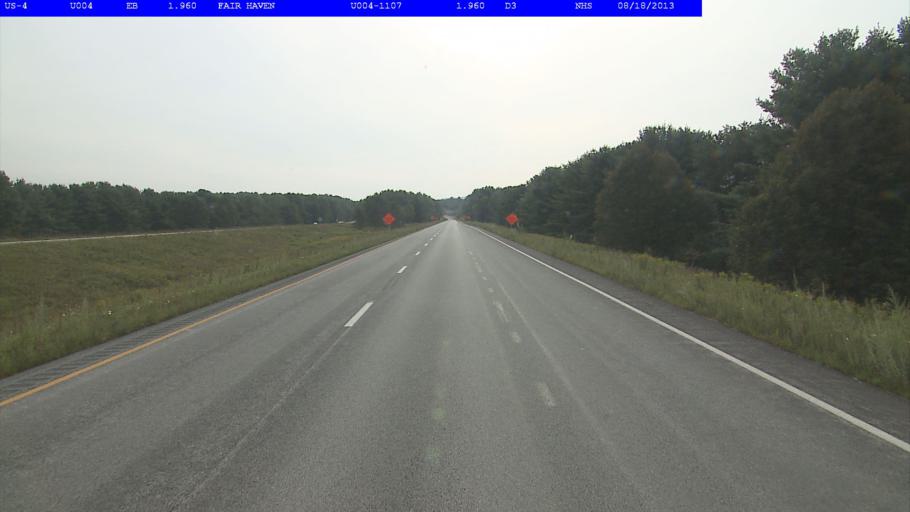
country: US
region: Vermont
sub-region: Rutland County
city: Fair Haven
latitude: 43.6058
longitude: -73.2723
